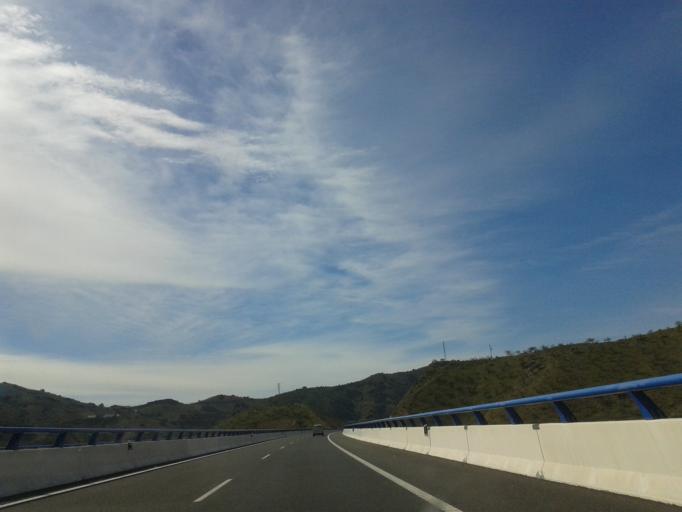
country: ES
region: Andalusia
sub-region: Provincia de Malaga
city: Casabermeja
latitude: 36.8879
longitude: -4.4698
